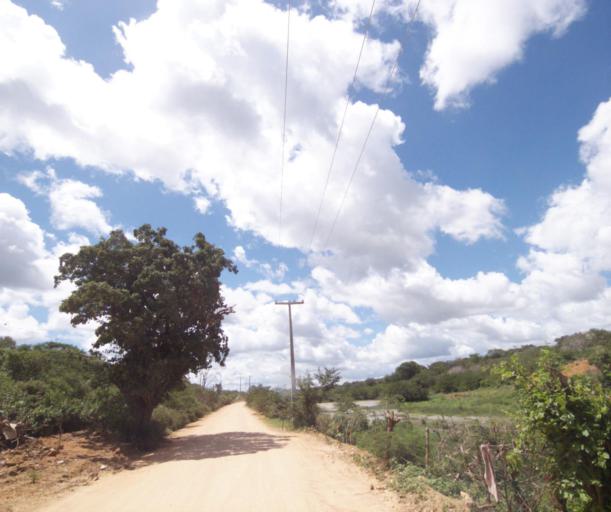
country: BR
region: Bahia
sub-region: Pocoes
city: Pocoes
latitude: -14.3557
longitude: -40.5874
